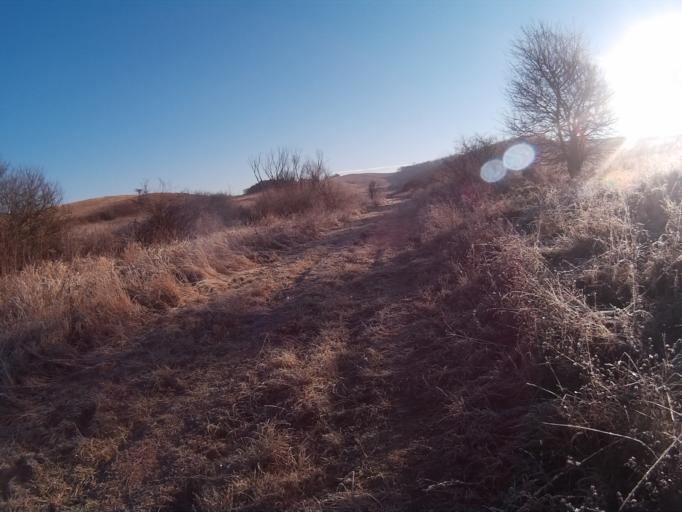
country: HU
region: Borsod-Abauj-Zemplen
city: Putnok
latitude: 48.3773
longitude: 20.4354
